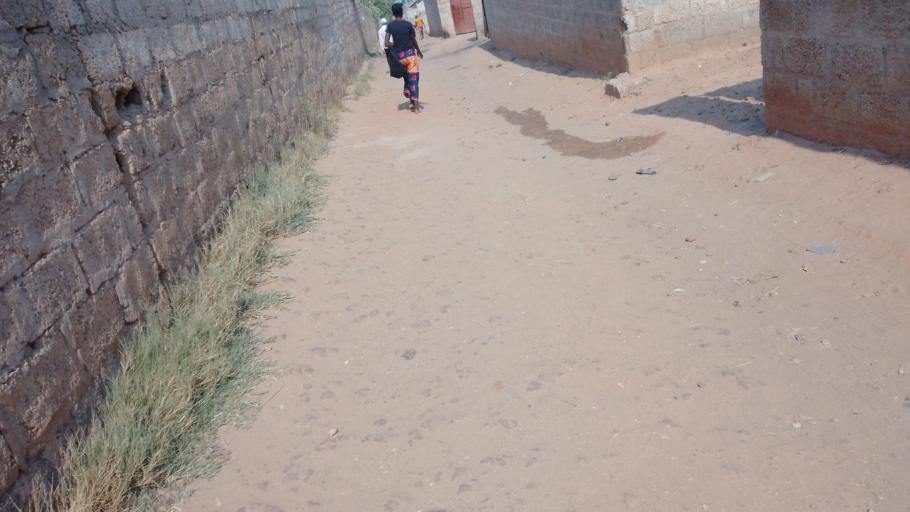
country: ZM
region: Lusaka
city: Lusaka
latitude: -15.4022
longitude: 28.3681
